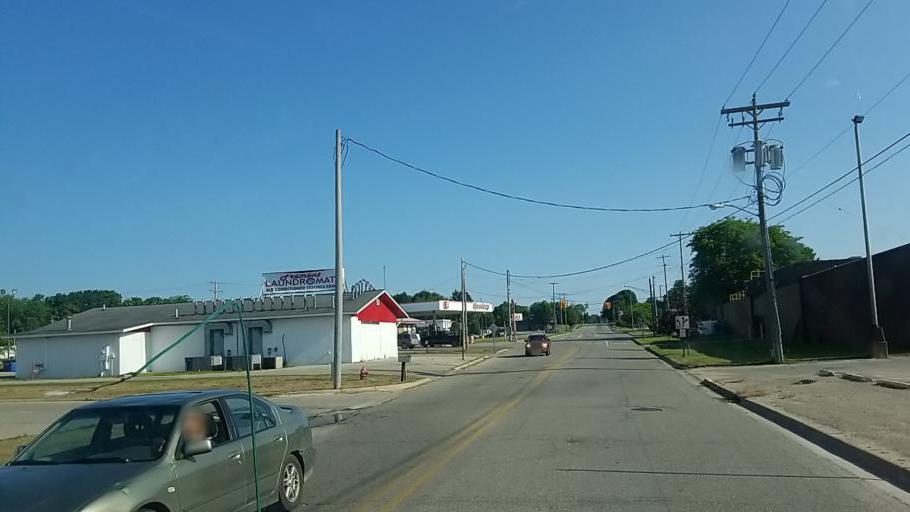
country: US
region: Michigan
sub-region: Newaygo County
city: Fremont
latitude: 43.4661
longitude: -85.9598
